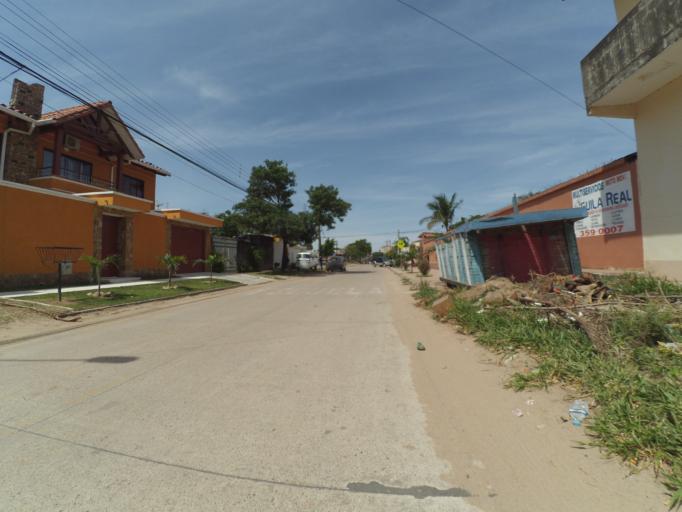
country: BO
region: Santa Cruz
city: Santa Cruz de la Sierra
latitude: -17.8101
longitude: -63.2125
